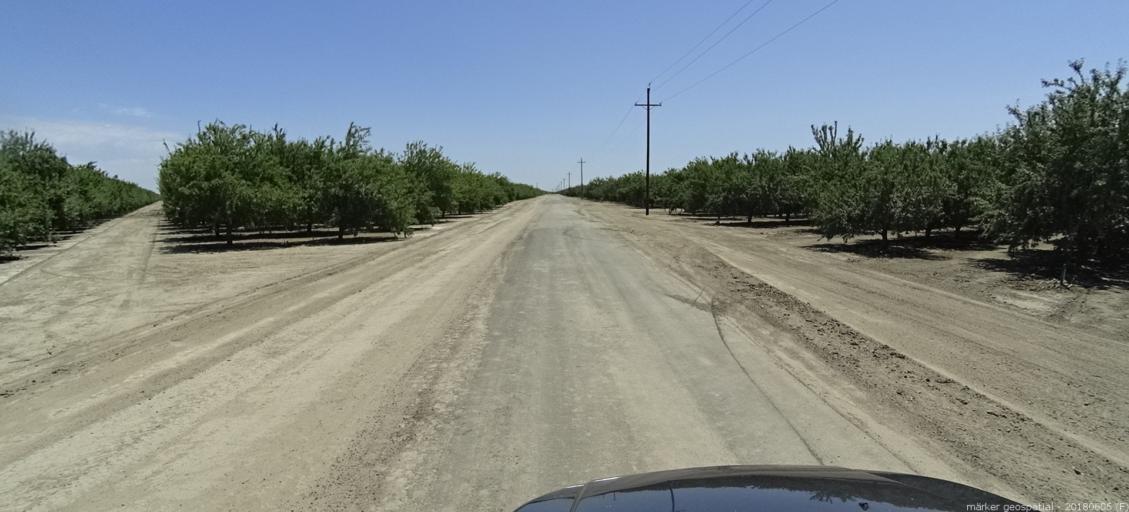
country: US
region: California
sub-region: Fresno County
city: Mendota
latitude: 36.7986
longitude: -120.3322
